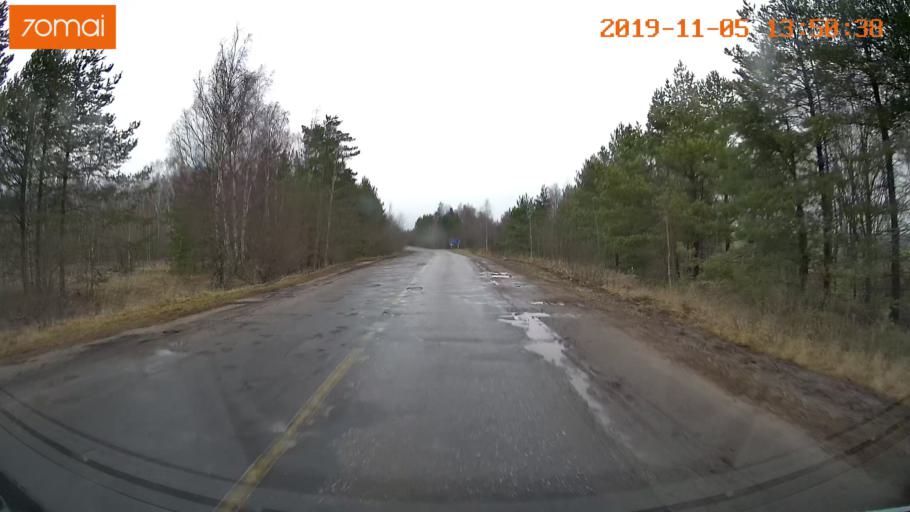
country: RU
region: Ivanovo
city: Kaminskiy
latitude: 57.0207
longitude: 41.4071
